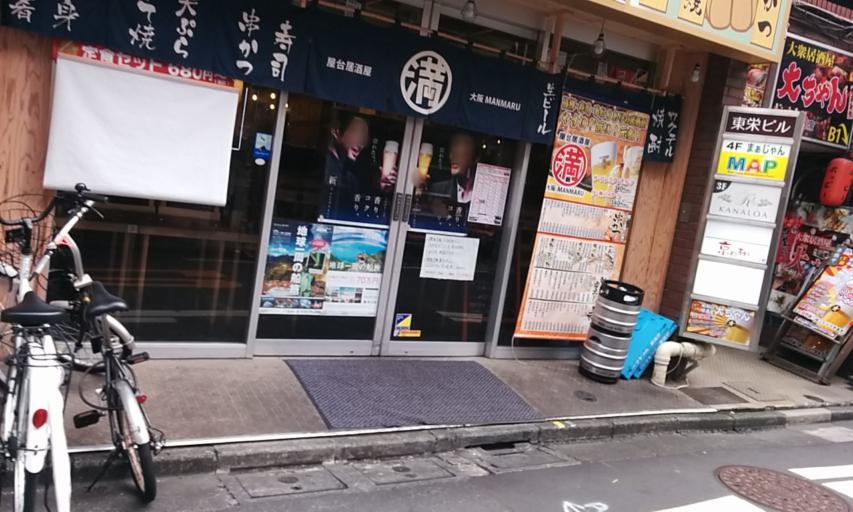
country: JP
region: Tokyo
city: Tokyo
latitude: 35.7143
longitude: 139.7035
